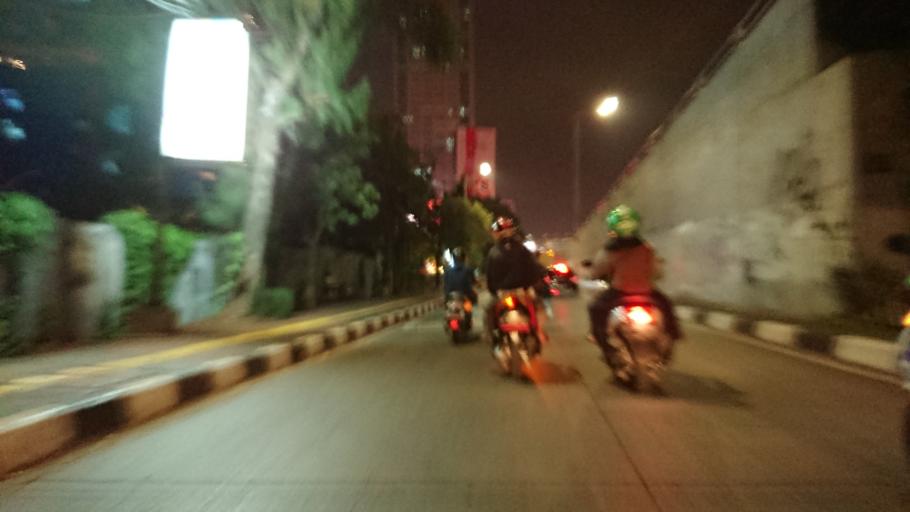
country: ID
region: Jakarta Raya
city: Jakarta
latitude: -6.2032
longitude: 106.8001
